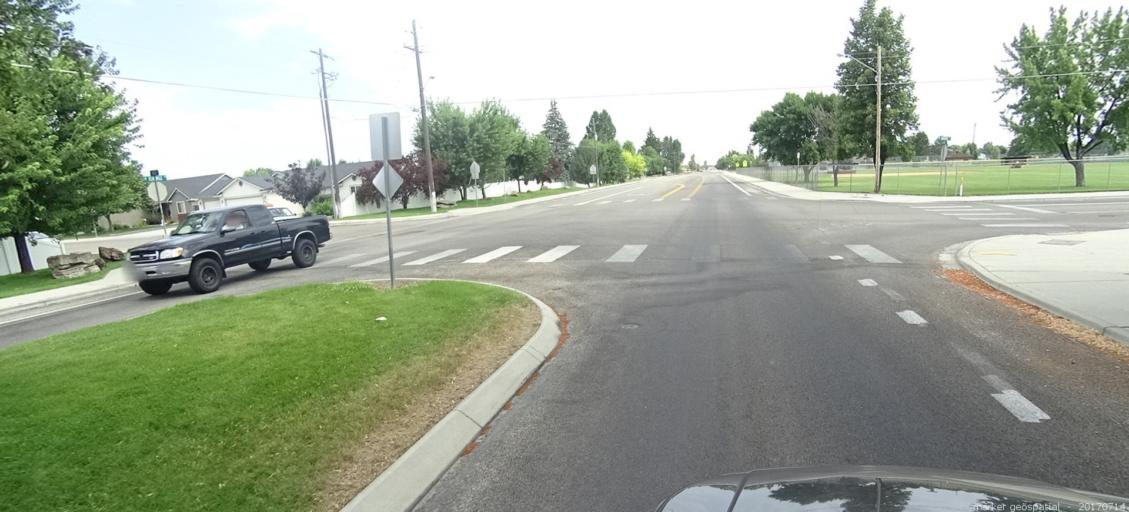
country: US
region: Idaho
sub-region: Ada County
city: Kuna
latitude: 43.4954
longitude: -116.4335
